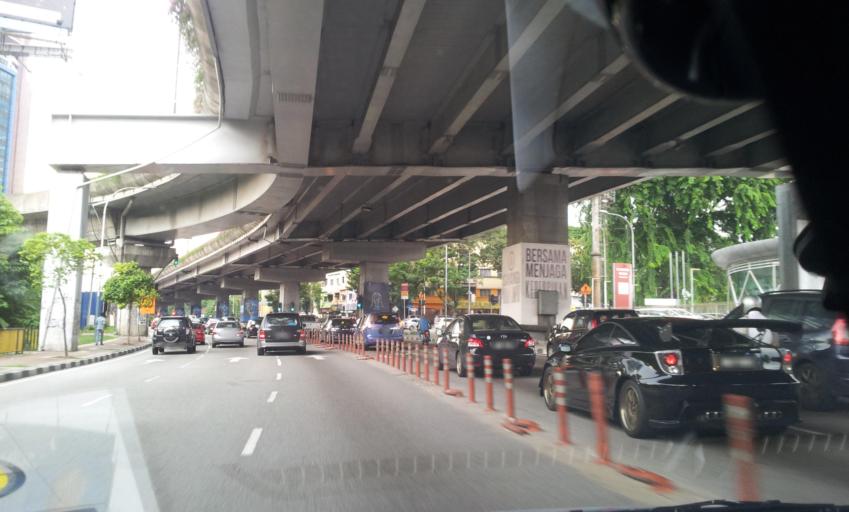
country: MY
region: Kuala Lumpur
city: Kuala Lumpur
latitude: 3.1662
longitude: 101.7146
